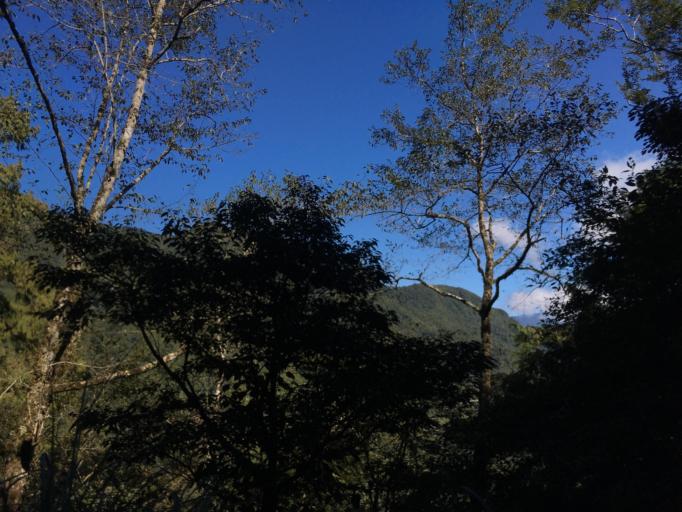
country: TW
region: Taiwan
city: Daxi
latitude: 24.5993
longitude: 121.4442
